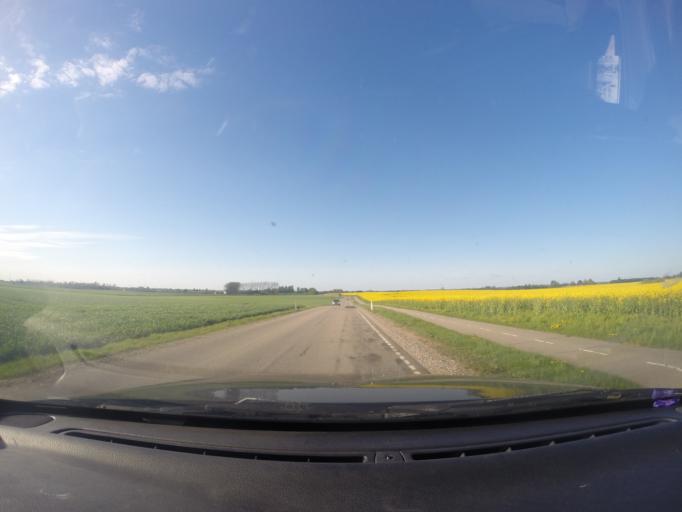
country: DK
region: Capital Region
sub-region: Hoje-Taastrup Kommune
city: Taastrup
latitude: 55.6716
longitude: 12.2538
